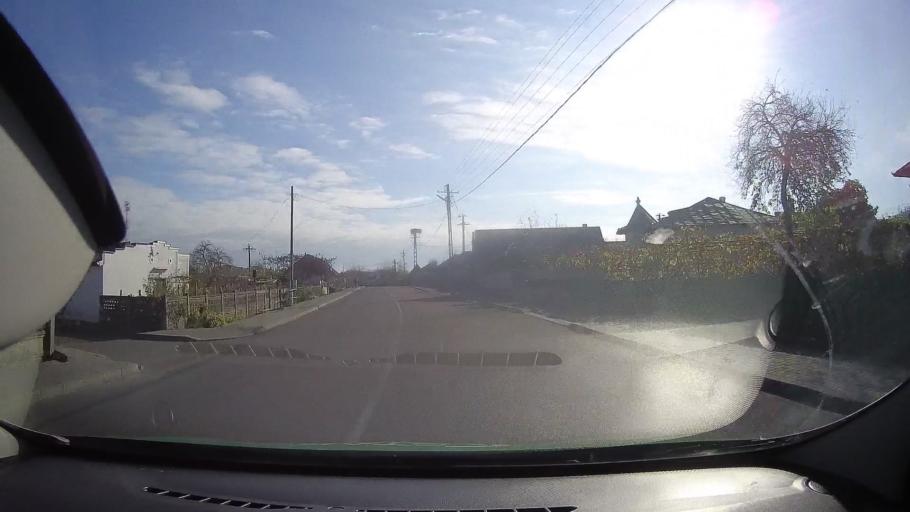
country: RO
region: Tulcea
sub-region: Comuna Murighiol
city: Murighiol
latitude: 45.0380
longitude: 29.1606
